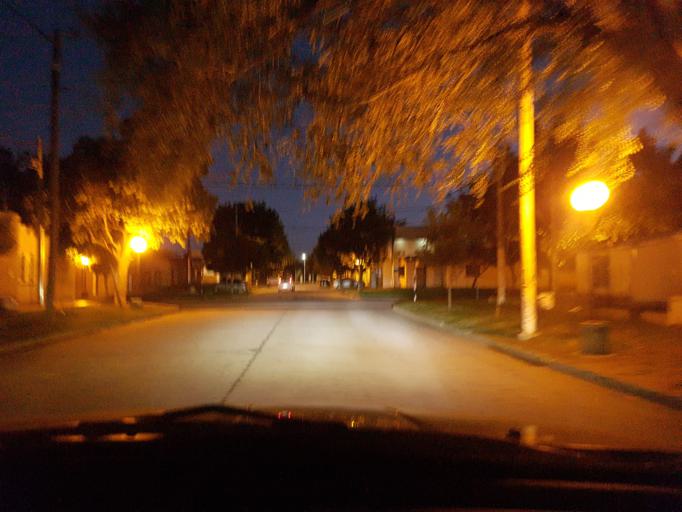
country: AR
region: Cordoba
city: Las Perdices
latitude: -32.7562
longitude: -63.7800
